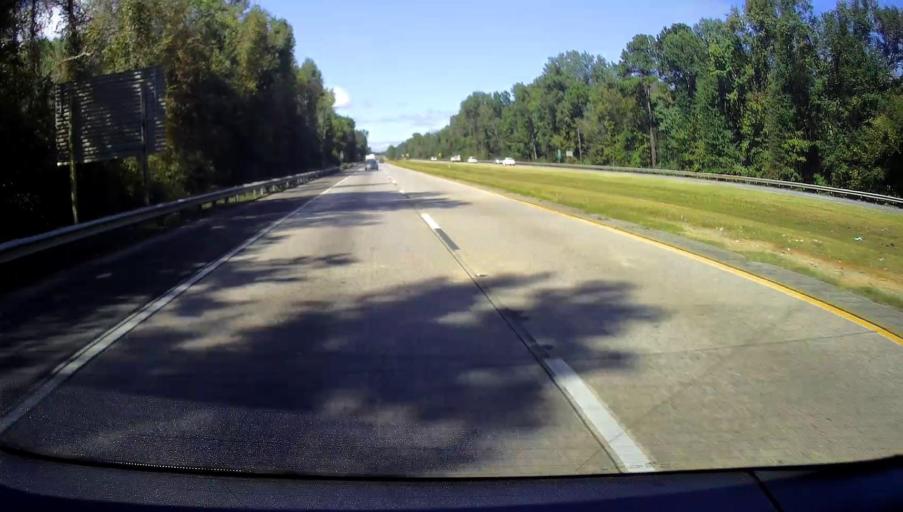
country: US
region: Georgia
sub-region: Bibb County
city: Macon
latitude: 32.8166
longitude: -83.5843
